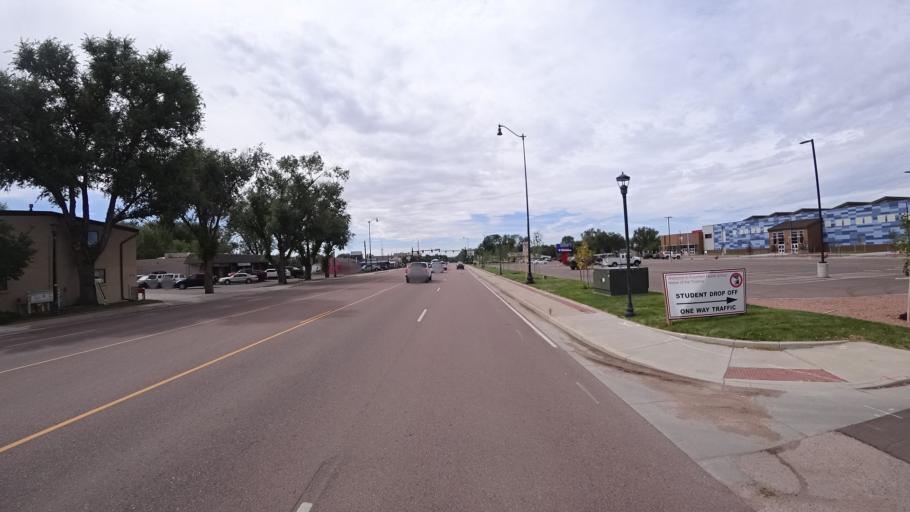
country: US
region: Colorado
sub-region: El Paso County
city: Fountain
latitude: 38.6870
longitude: -104.7047
